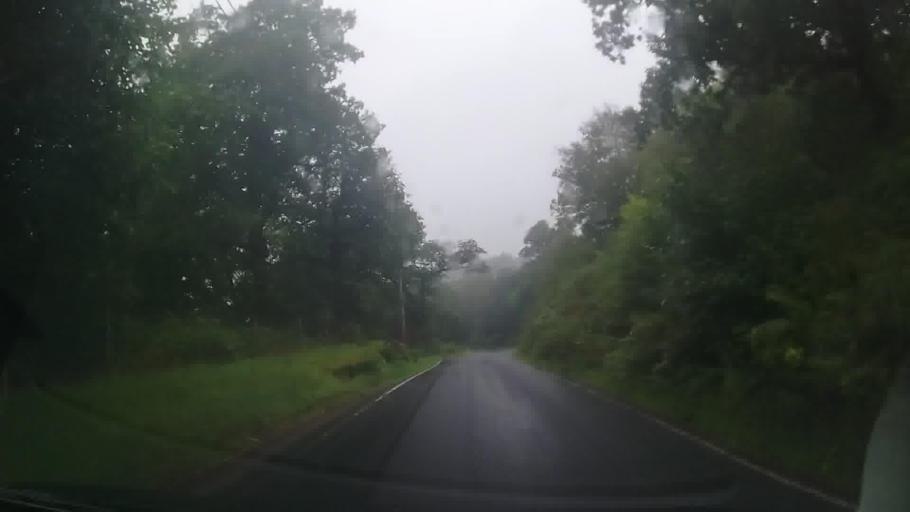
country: GB
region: Scotland
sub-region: Argyll and Bute
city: Isle Of Mull
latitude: 56.6853
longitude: -5.6327
